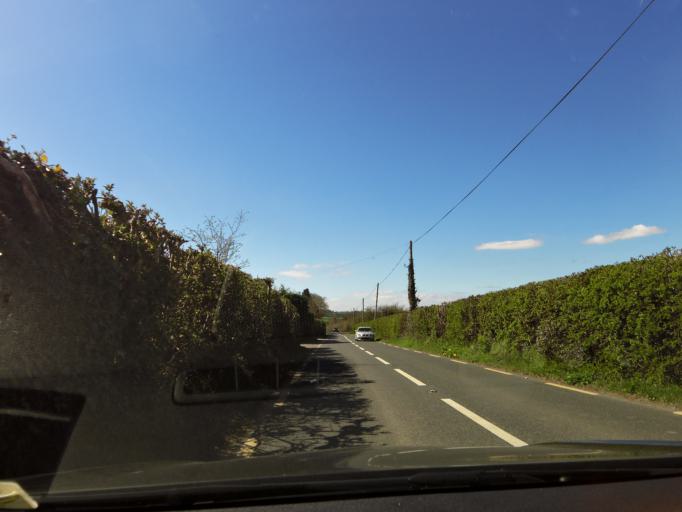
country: IE
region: Leinster
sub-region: Kildare
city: Moone
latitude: 53.0003
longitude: -6.8012
